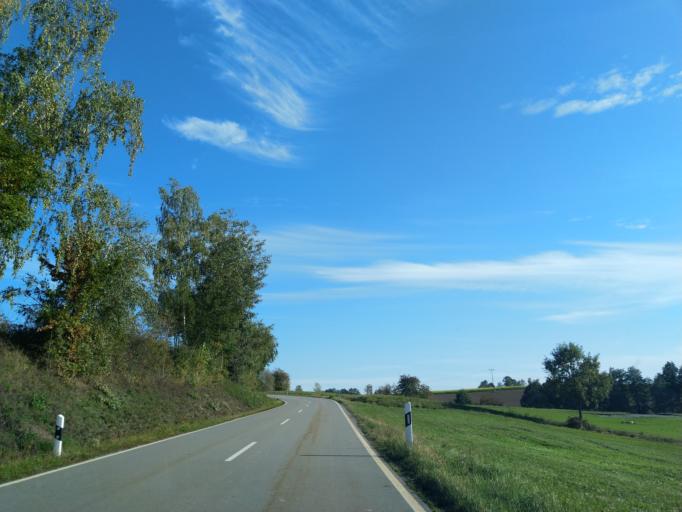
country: DE
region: Bavaria
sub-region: Lower Bavaria
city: Schwarzach
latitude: 48.9035
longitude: 12.8336
